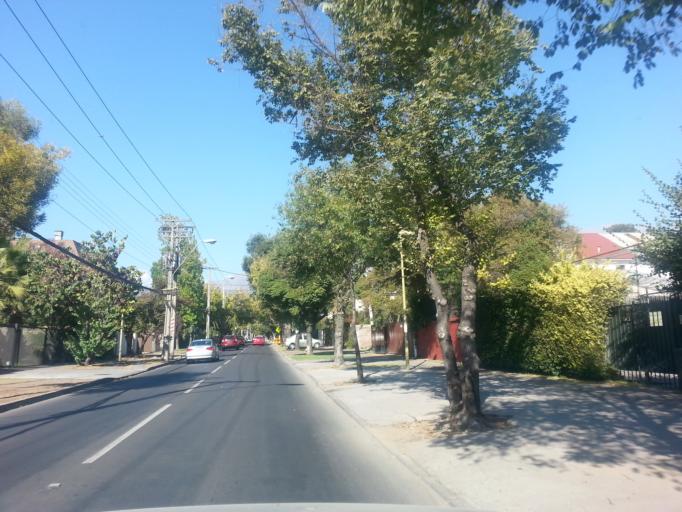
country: CL
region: Santiago Metropolitan
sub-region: Provincia de Santiago
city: Villa Presidente Frei, Nunoa, Santiago, Chile
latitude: -33.4261
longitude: -70.5723
